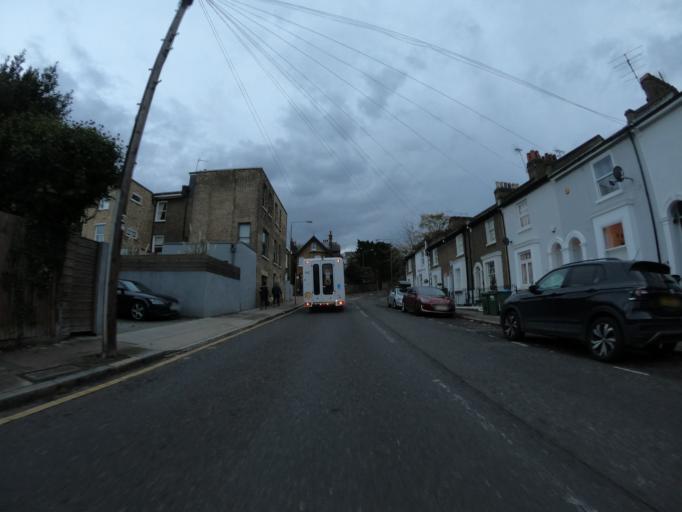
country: GB
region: England
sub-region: Greater London
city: Blackheath
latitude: 51.4839
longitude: 0.0085
